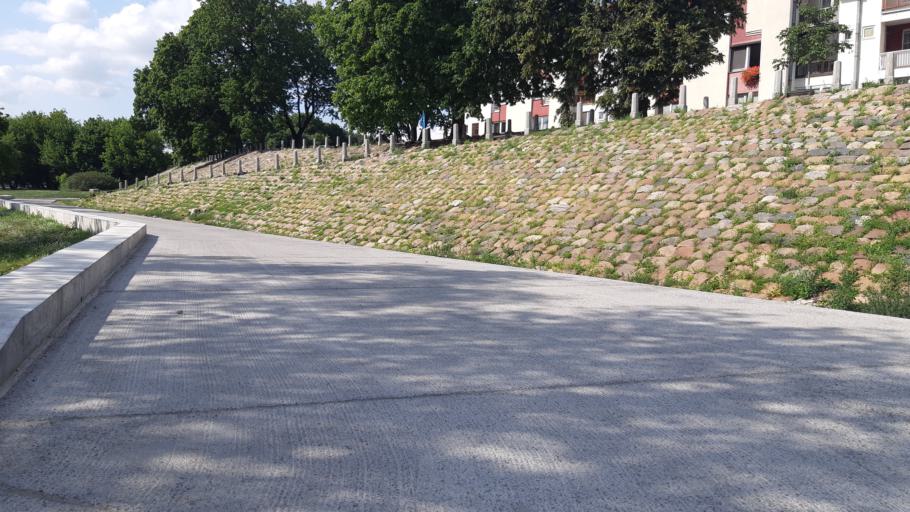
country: LT
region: Kauno apskritis
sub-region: Kaunas
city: Kaunas
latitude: 54.8950
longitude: 23.8830
